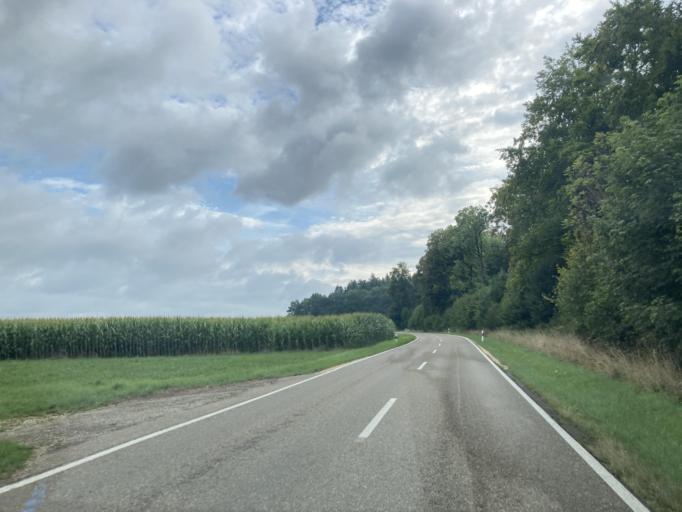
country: DE
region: Bavaria
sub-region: Swabia
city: Medlingen
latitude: 48.5853
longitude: 10.3085
